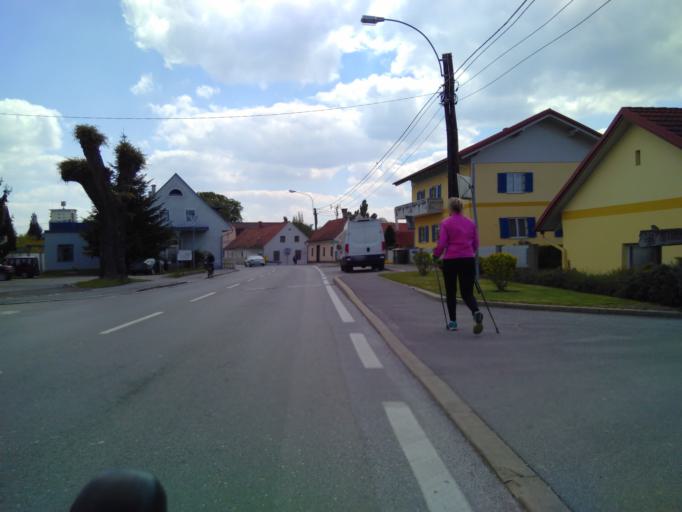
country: AT
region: Styria
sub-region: Politischer Bezirk Graz-Umgebung
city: Feldkirchen bei Graz
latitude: 47.0240
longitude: 15.4686
